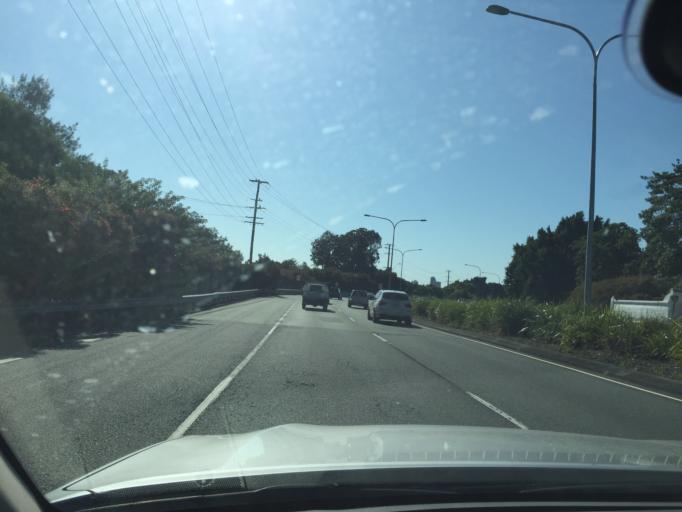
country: AU
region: Queensland
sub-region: Gold Coast
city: Clear Island Waters
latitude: -28.0312
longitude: 153.3946
